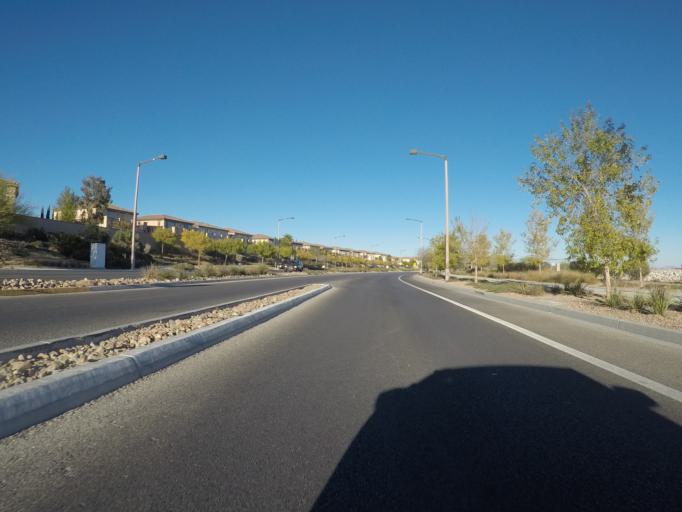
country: US
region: Nevada
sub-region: Clark County
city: Summerlin South
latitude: 36.1578
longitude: -115.3608
